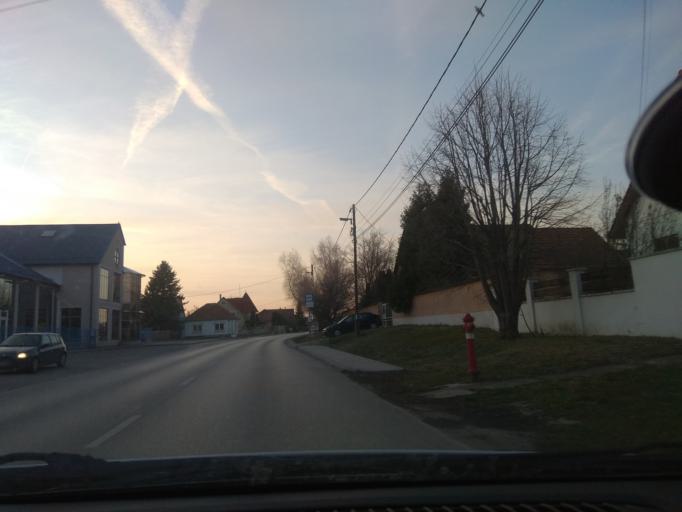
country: HU
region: Pest
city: Szigetszentmiklos
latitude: 47.3546
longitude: 19.0359
